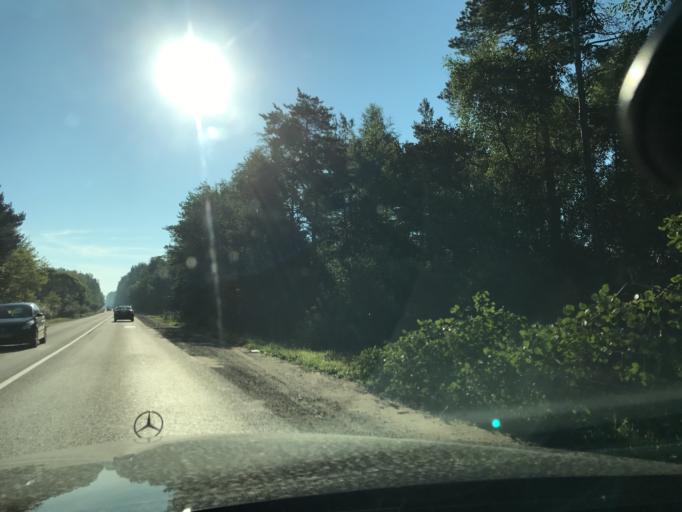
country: RU
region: Moskovskaya
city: Medvezh'i Ozera
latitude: 55.8593
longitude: 38.0043
